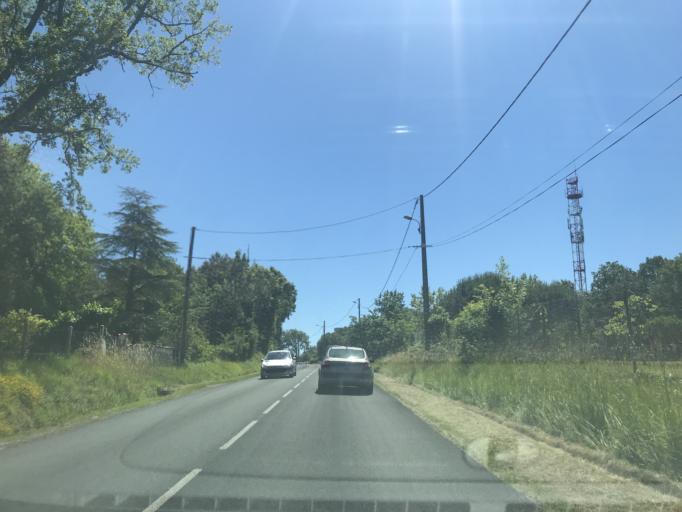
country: FR
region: Poitou-Charentes
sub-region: Departement de la Charente-Maritime
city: Meschers-sur-Gironde
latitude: 45.5682
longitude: -0.9611
